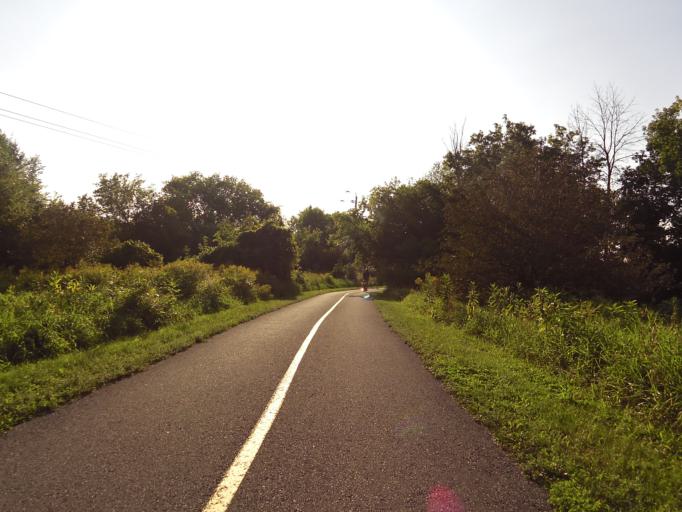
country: CA
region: Ontario
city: Bells Corners
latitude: 45.3427
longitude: -75.8760
